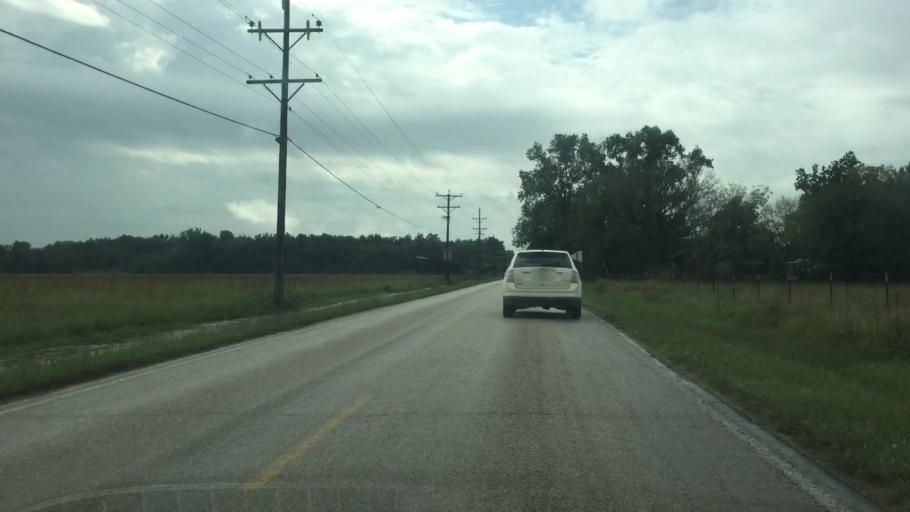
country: US
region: Kansas
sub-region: Allen County
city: Humboldt
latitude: 37.8719
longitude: -95.4369
